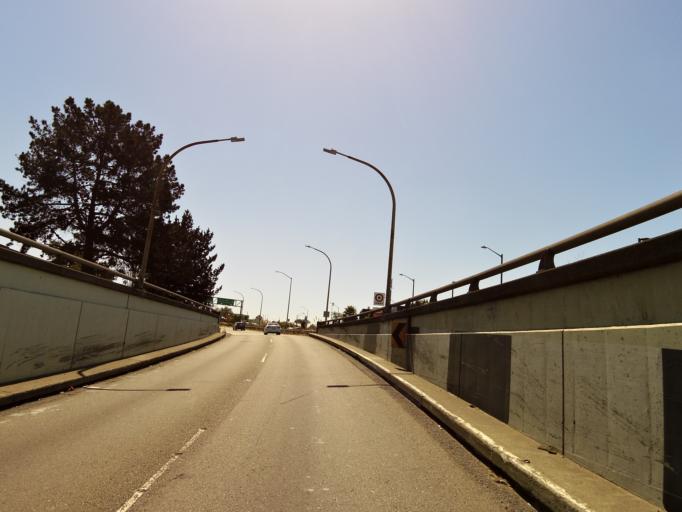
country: US
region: California
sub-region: Alameda County
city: Oakland
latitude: 37.7871
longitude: -122.2785
